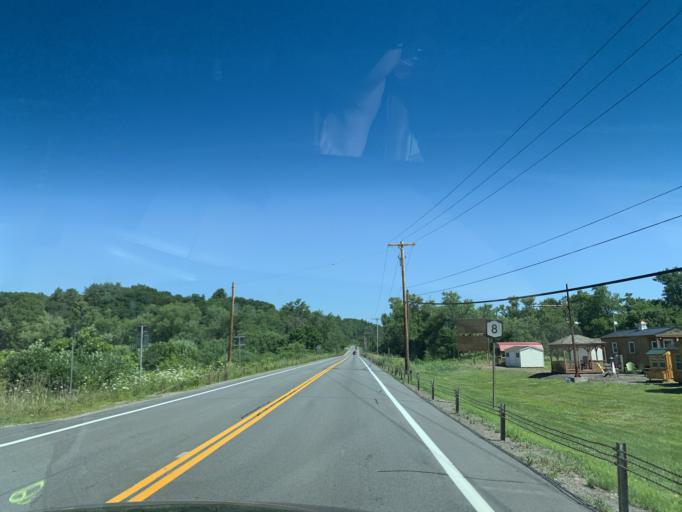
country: US
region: New York
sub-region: Delaware County
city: Sidney
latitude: 42.3187
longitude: -75.4120
